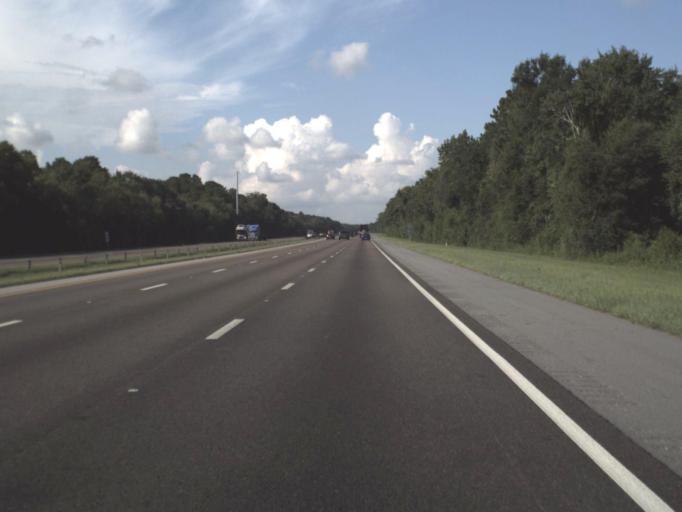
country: US
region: Florida
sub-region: Hillsborough County
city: Lutz
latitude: 28.1338
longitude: -82.4142
